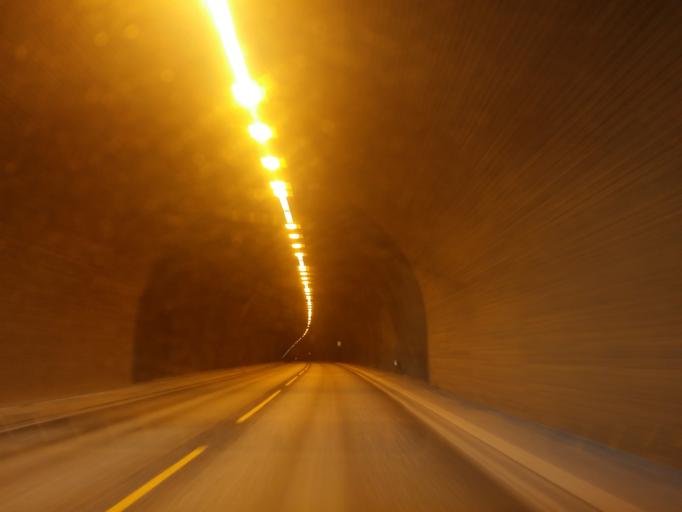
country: NO
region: Hordaland
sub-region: Granvin
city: Granvin
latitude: 60.5847
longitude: 6.6144
